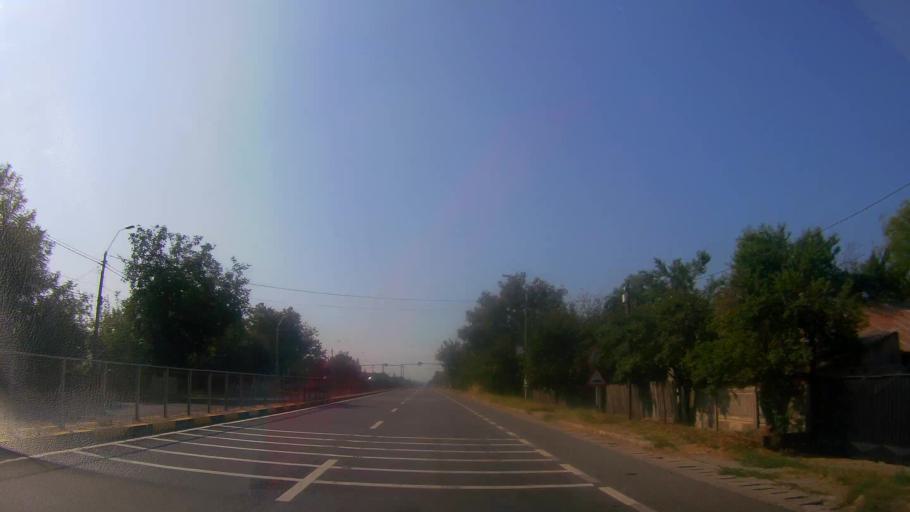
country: RO
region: Giurgiu
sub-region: Comuna Daia
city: Daia
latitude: 43.9858
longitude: 25.9898
